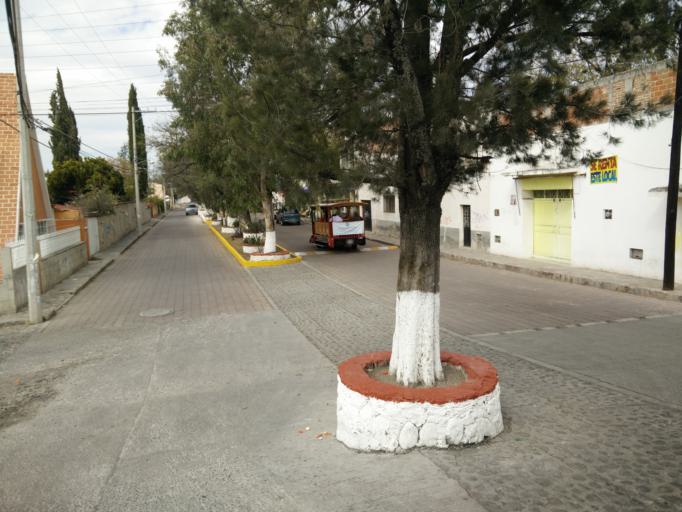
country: MX
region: Queretaro
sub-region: Tequisquiapan
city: Tequisquiapan
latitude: 20.5174
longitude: -99.8820
